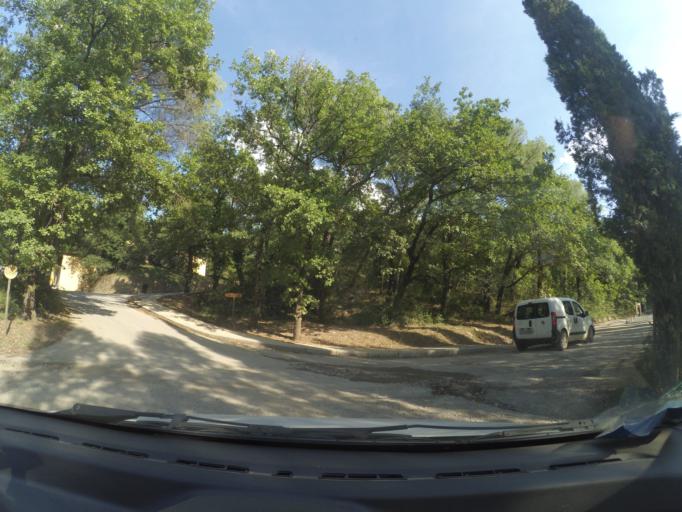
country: IT
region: Tuscany
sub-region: Province of Arezzo
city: Castiglion Fibocchi
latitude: 43.5294
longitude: 11.7783
